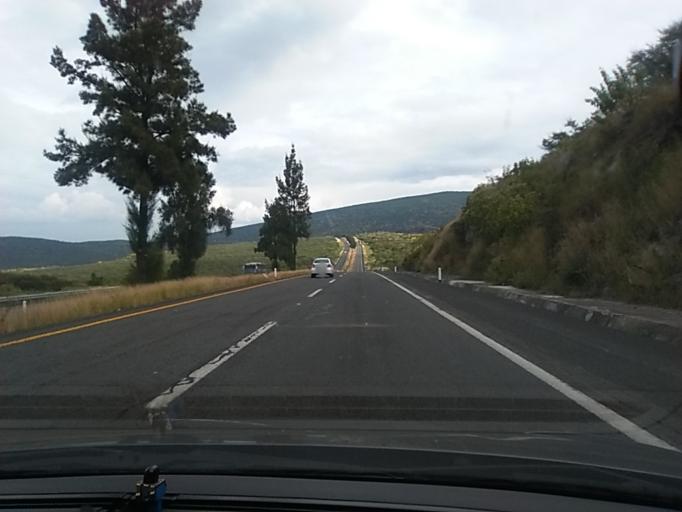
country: MX
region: Michoacan
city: Ixtlan
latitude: 20.2187
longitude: -102.3642
